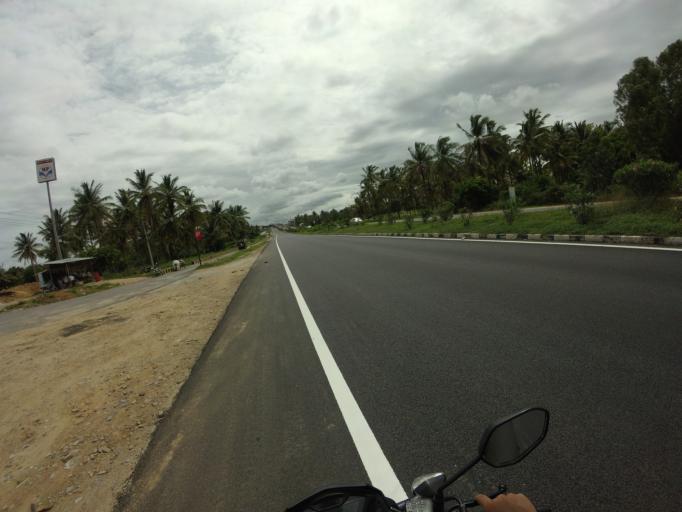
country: IN
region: Karnataka
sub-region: Mandya
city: Belluru
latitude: 12.9627
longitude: 76.7492
